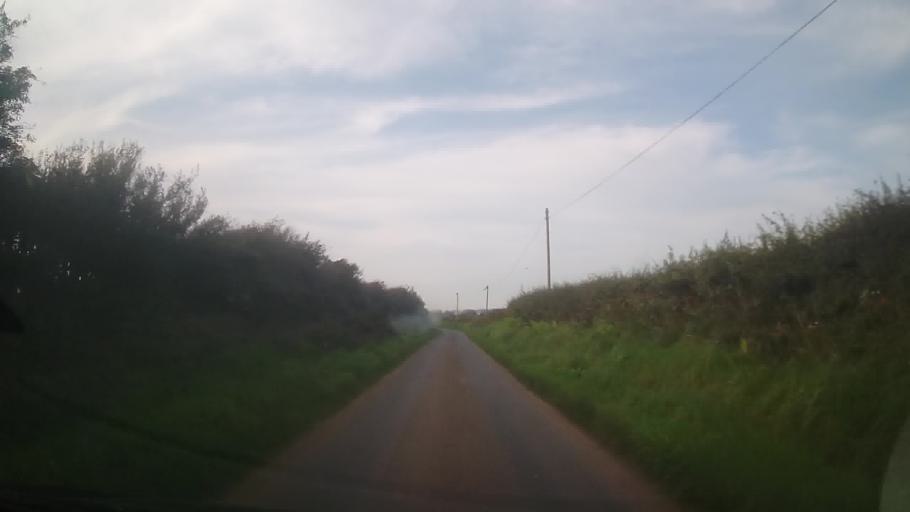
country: GB
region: Wales
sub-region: Pembrokeshire
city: Camrose
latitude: 51.8838
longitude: -5.0521
